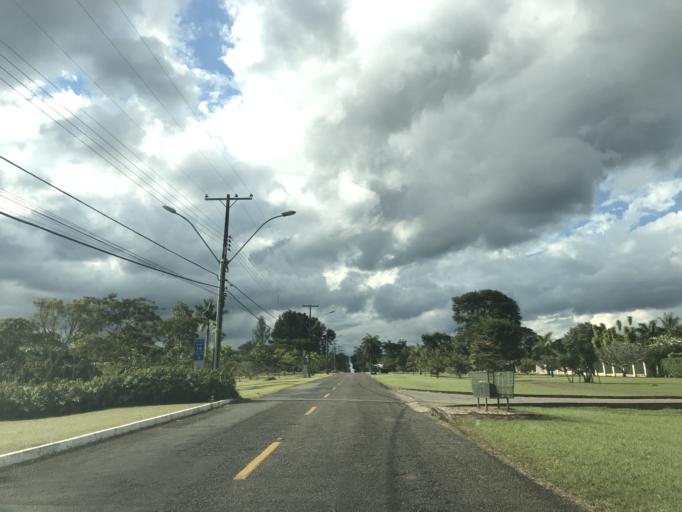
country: BR
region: Federal District
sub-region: Brasilia
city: Brasilia
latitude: -15.9125
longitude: -47.9414
